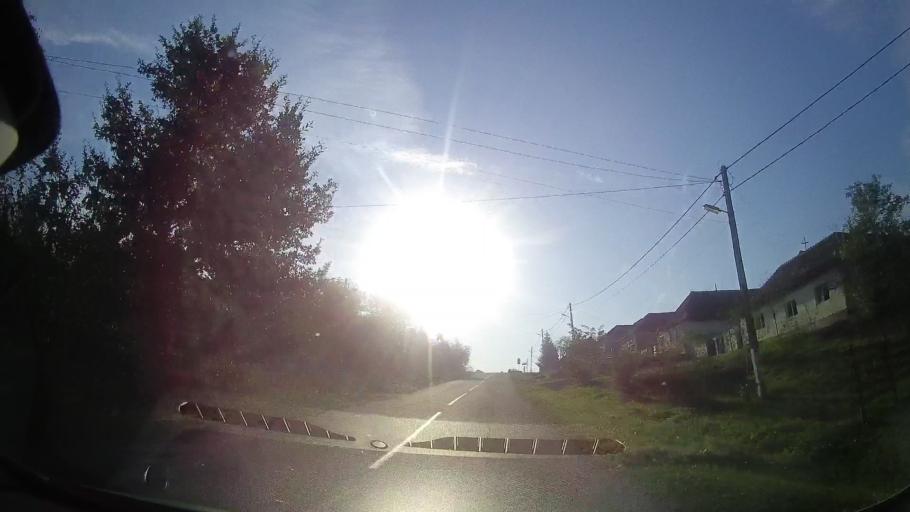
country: RO
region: Timis
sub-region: Comuna Bogda
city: Bogda
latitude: 45.9806
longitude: 21.5729
